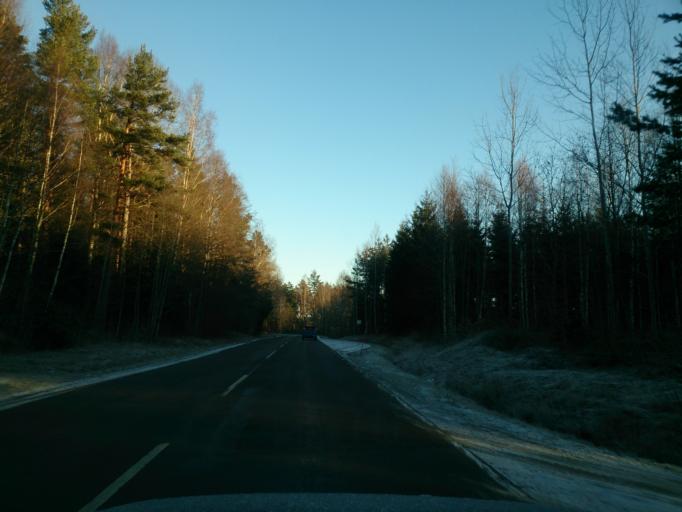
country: SE
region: OEstergoetland
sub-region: Norrkopings Kommun
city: Kimstad
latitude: 58.3747
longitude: 16.0267
